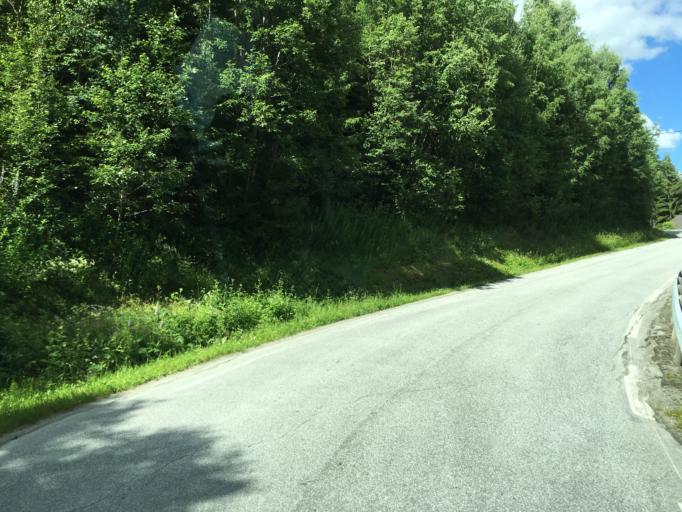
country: NO
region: Oppland
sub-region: Sondre Land
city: Hov
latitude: 60.6795
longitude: 10.3102
